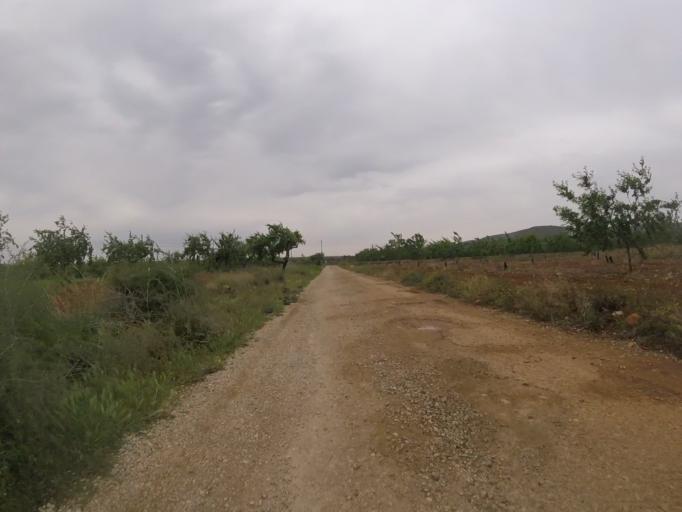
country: ES
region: Valencia
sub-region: Provincia de Castello
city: Alcoceber
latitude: 40.2661
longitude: 0.2553
